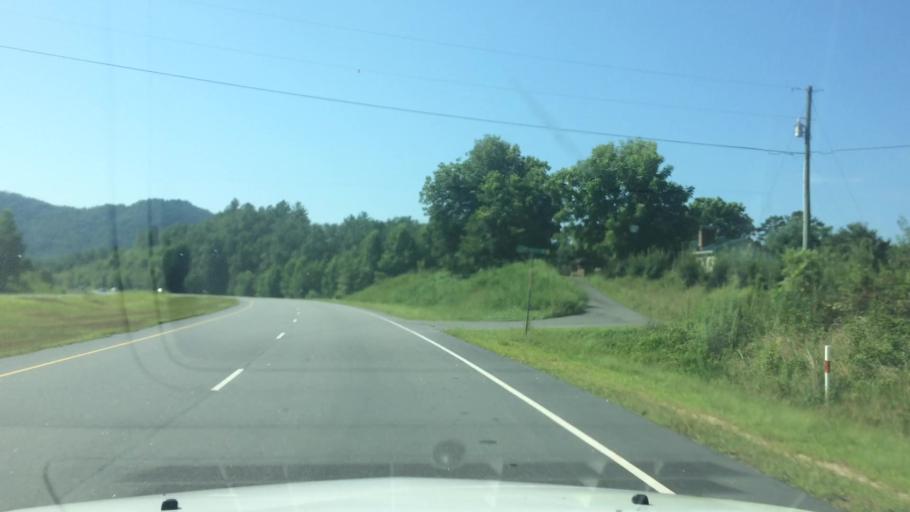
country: US
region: North Carolina
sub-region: Caldwell County
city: Lenoir
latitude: 35.9892
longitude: -81.5723
